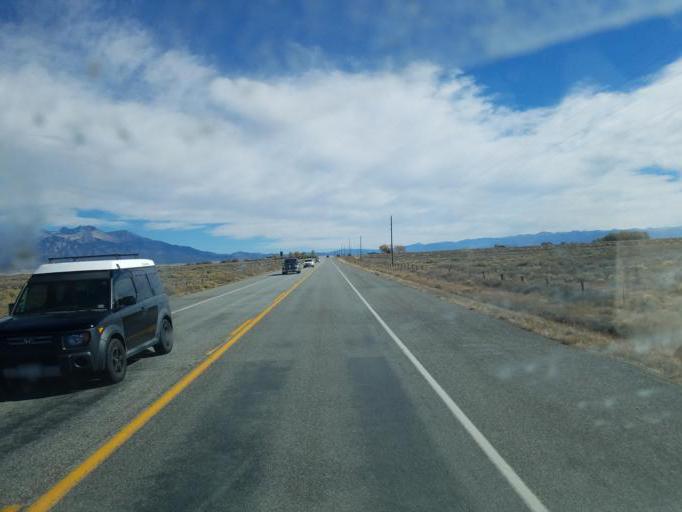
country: US
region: Colorado
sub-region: Alamosa County
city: Alamosa East
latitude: 37.4742
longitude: -105.7457
